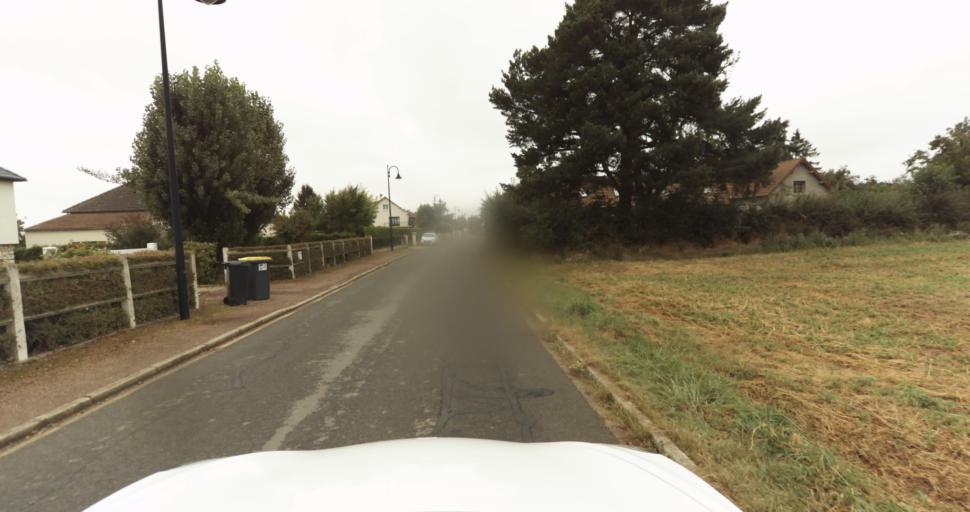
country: FR
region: Haute-Normandie
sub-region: Departement de l'Eure
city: Aviron
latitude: 49.0735
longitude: 1.0920
